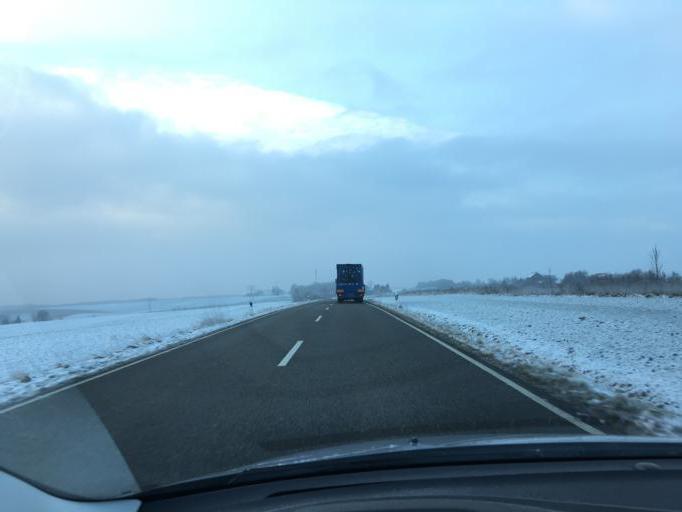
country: DE
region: Saxony
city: Narsdorf
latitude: 50.9770
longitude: 12.6975
